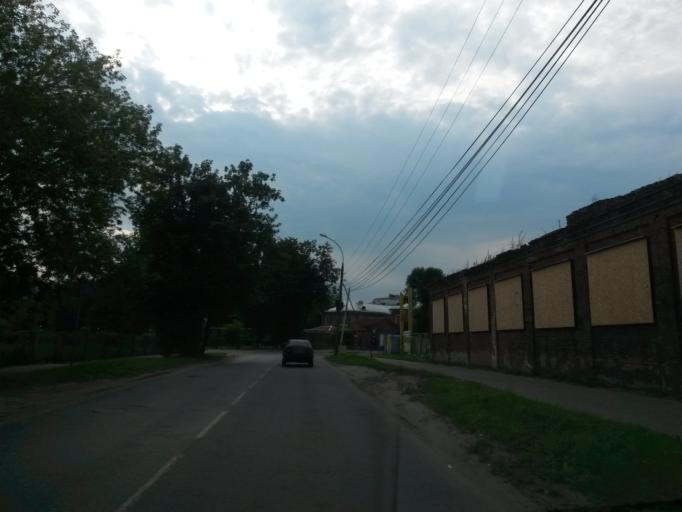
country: RU
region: Jaroslavl
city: Yaroslavl
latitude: 57.6084
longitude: 39.8319
